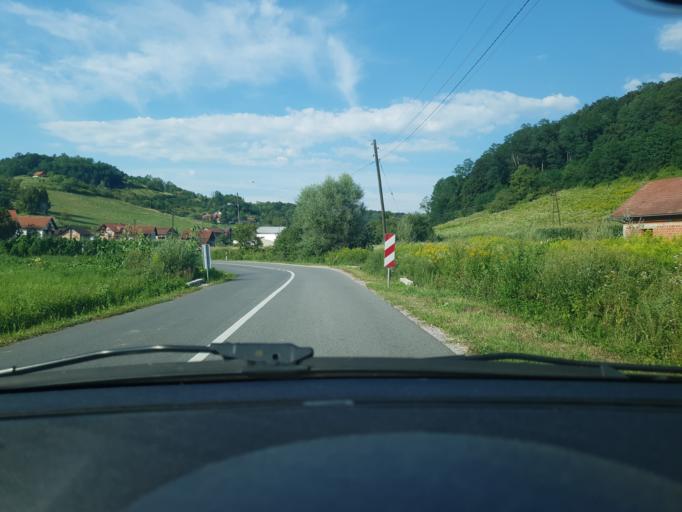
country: HR
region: Krapinsko-Zagorska
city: Pregrada
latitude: 46.0829
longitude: 15.8106
